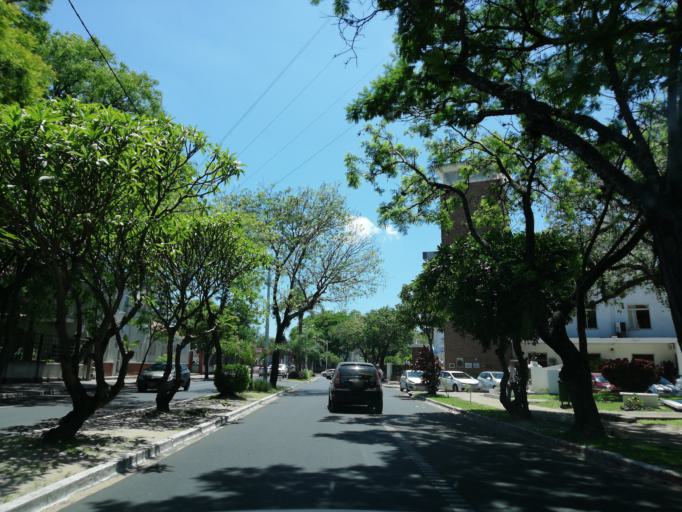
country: AR
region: Corrientes
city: Corrientes
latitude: -27.4616
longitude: -58.8359
